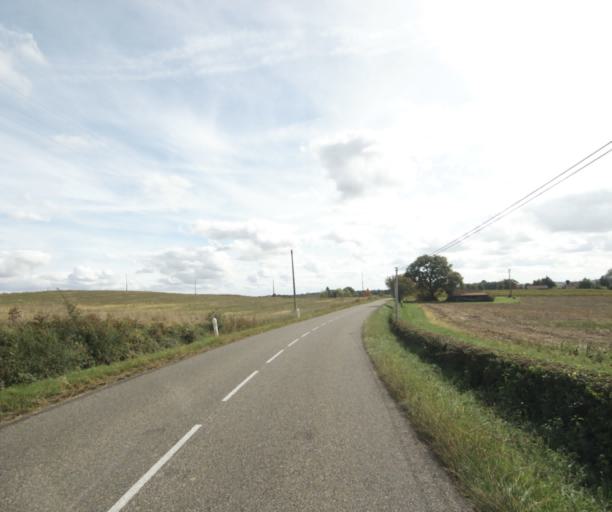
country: FR
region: Midi-Pyrenees
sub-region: Departement du Gers
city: Eauze
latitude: 43.8416
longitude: 0.1502
